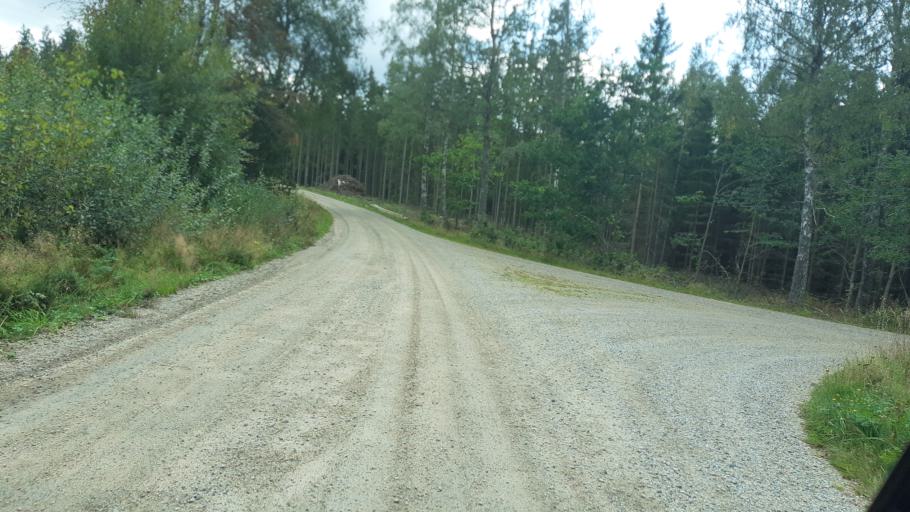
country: SE
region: Kronoberg
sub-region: Tingsryds Kommun
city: Tingsryd
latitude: 56.4456
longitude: 15.1680
